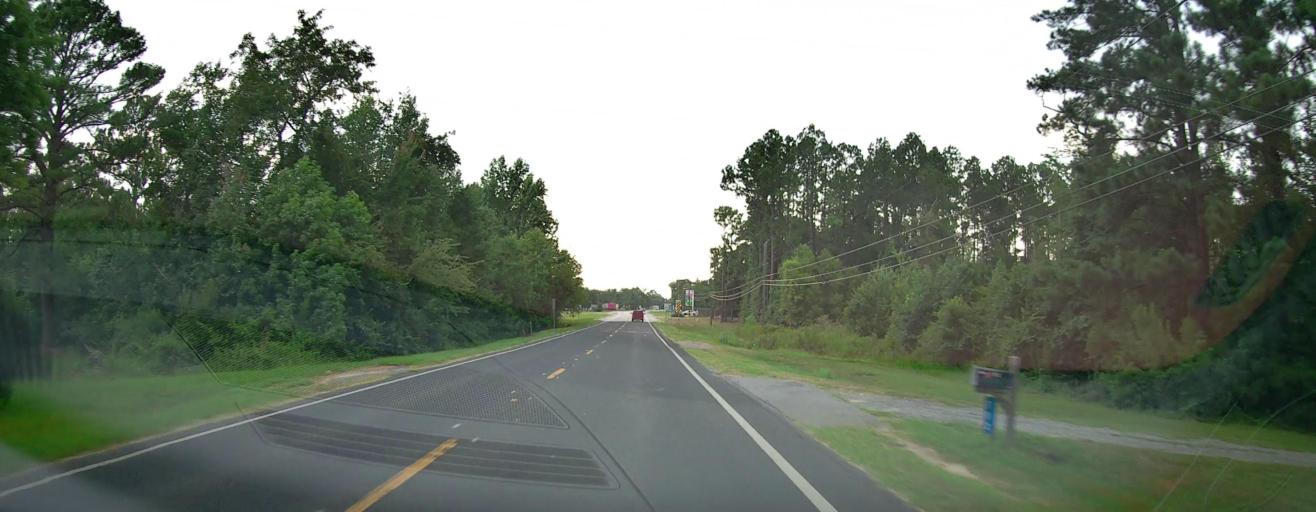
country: US
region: Georgia
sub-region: Laurens County
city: East Dublin
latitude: 32.5406
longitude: -82.8582
